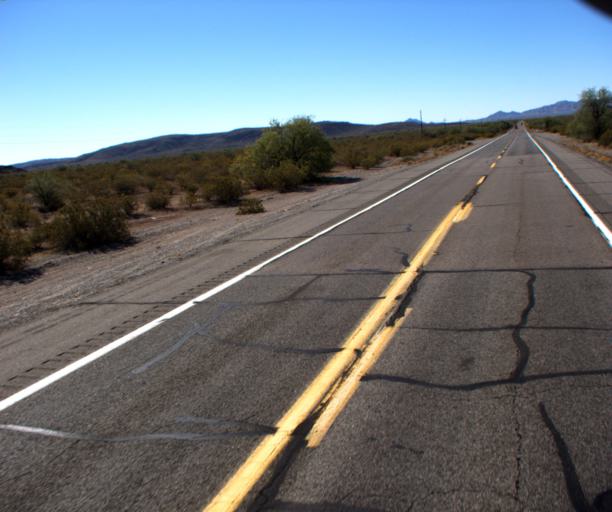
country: US
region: Arizona
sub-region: Pima County
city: Ajo
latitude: 32.5371
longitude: -112.8801
